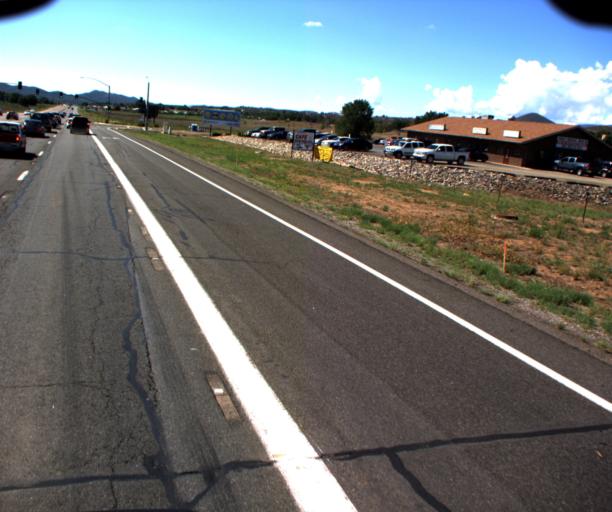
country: US
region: Arizona
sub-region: Yavapai County
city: Dewey-Humboldt
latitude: 34.5483
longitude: -112.2506
